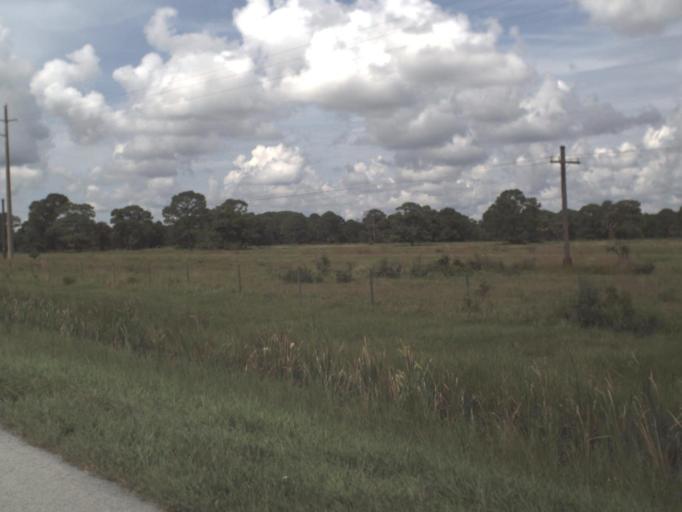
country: US
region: Florida
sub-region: Glades County
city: Buckhead Ridge
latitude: 27.2363
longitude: -80.9945
